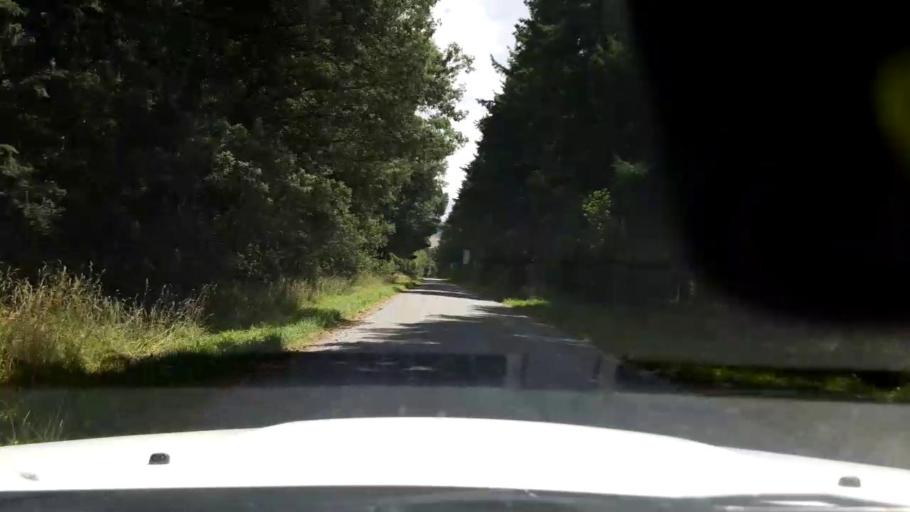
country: NZ
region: Canterbury
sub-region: Timaru District
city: Pleasant Point
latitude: -43.9691
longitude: 171.2331
